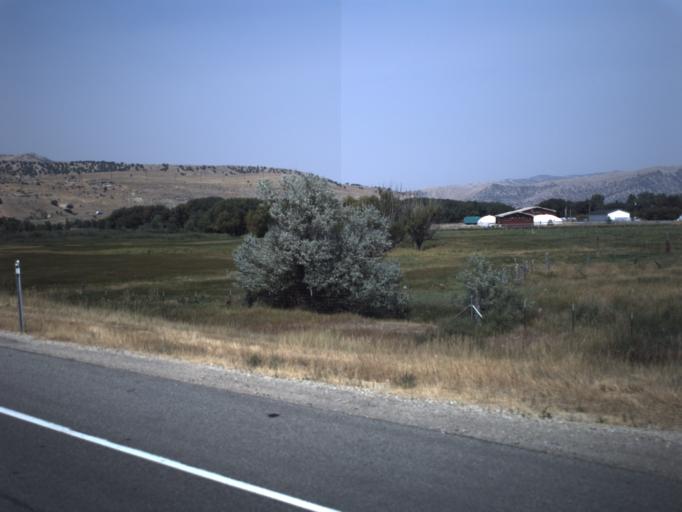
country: US
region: Utah
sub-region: Summit County
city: Coalville
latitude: 40.9135
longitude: -111.4014
